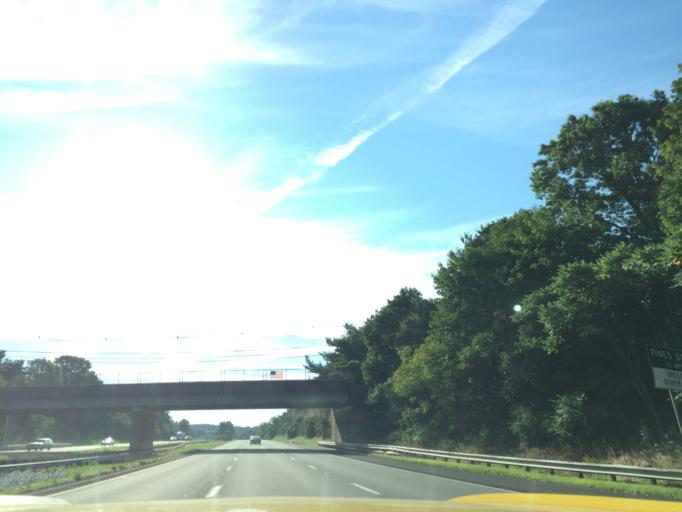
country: US
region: New Jersey
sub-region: Hunterdon County
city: Lebanon
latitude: 40.6465
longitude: -74.8215
